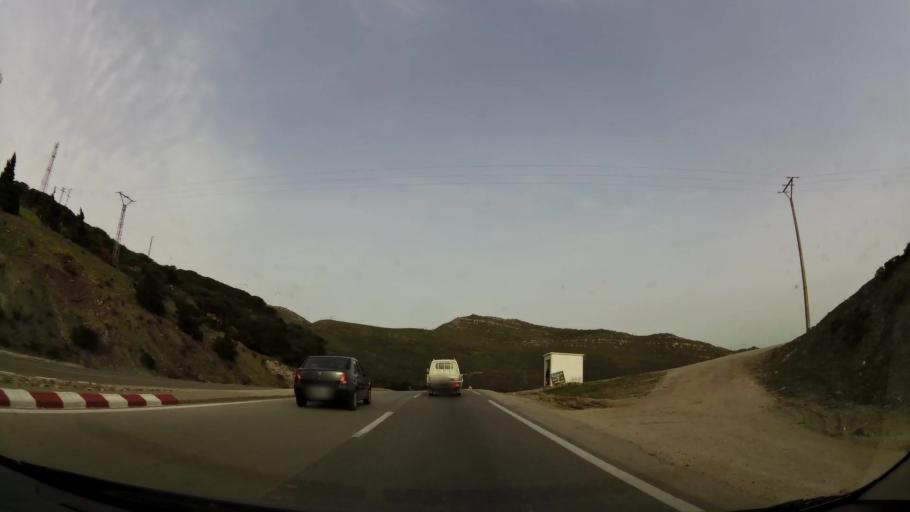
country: MA
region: Tanger-Tetouan
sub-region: Tetouan
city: Saddina
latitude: 35.5603
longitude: -5.5737
